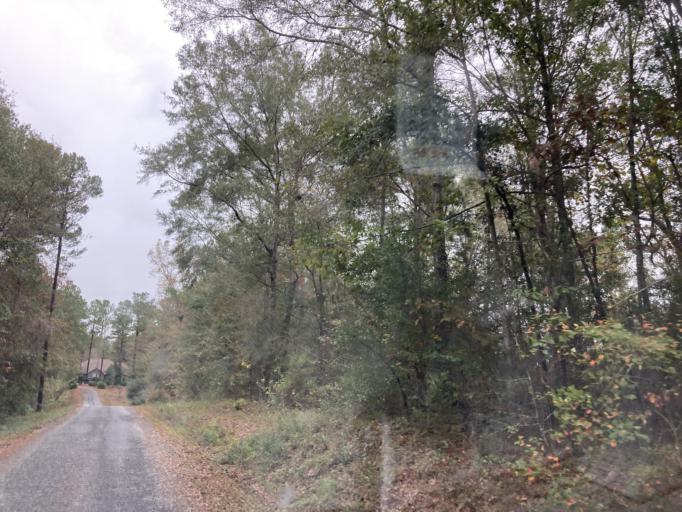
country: US
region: Mississippi
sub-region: Lamar County
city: Purvis
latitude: 31.1904
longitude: -89.4242
